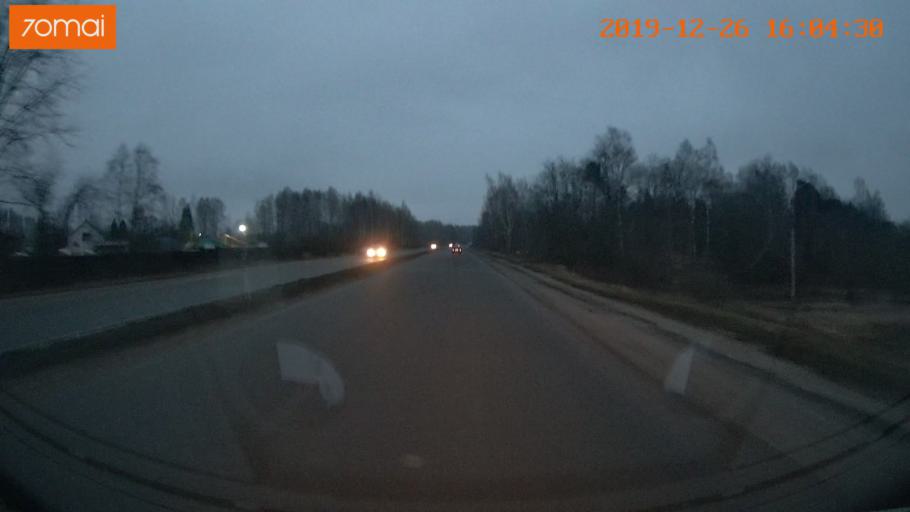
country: RU
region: Jaroslavl
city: Rybinsk
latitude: 58.0084
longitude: 38.8719
